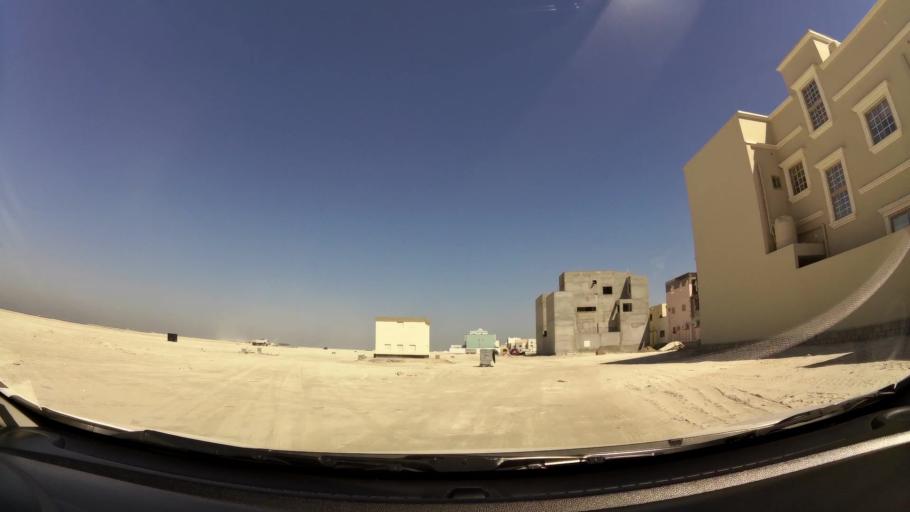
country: BH
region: Muharraq
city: Al Muharraq
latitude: 26.2705
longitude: 50.5950
